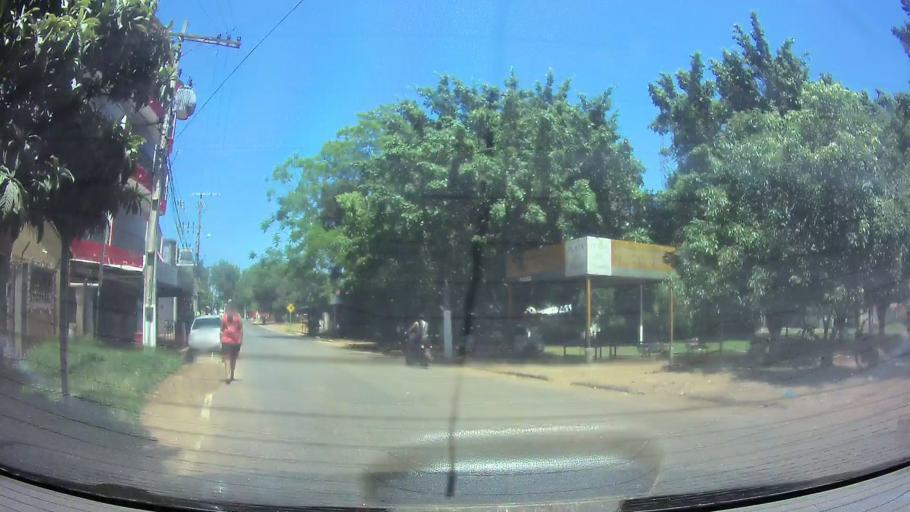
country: PY
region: Central
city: San Lorenzo
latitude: -25.3329
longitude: -57.4842
